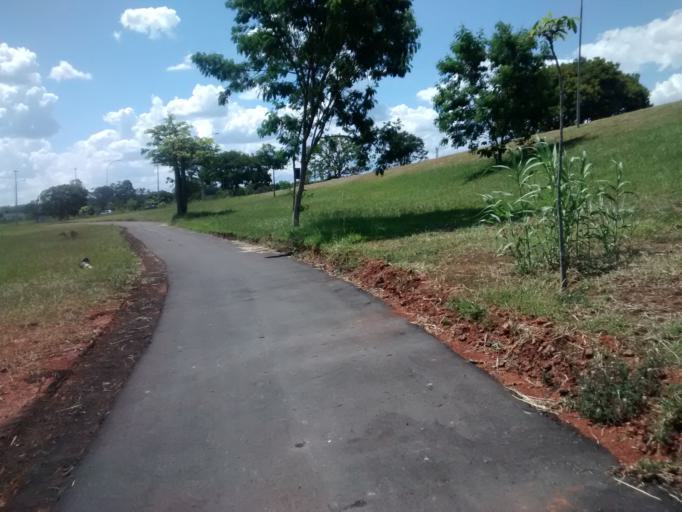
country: BR
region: Federal District
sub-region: Brasilia
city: Brasilia
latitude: -15.7770
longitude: -47.8639
